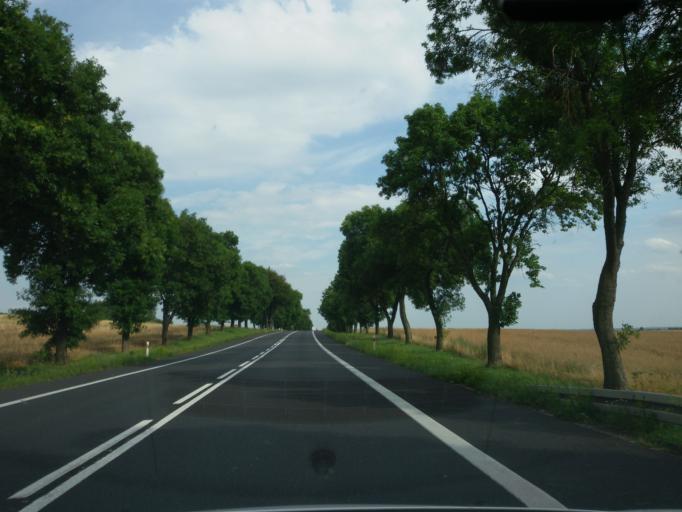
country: PL
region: Lower Silesian Voivodeship
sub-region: Powiat polkowicki
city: Gaworzyce
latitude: 51.6424
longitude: 15.8769
